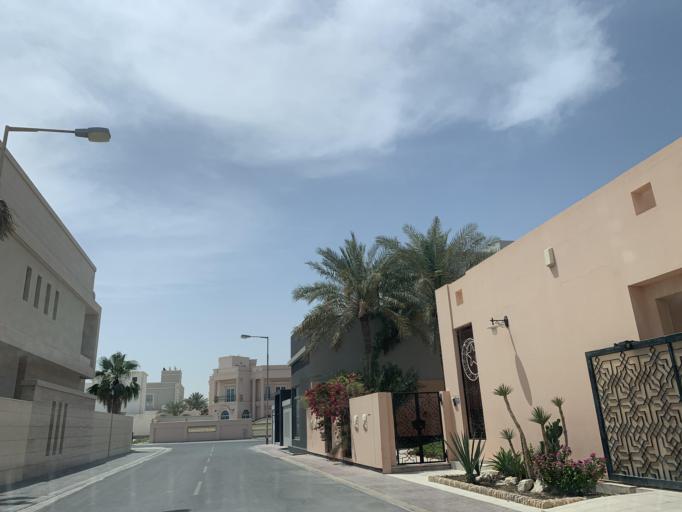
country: BH
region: Northern
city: Ar Rifa'
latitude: 26.1438
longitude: 50.5561
